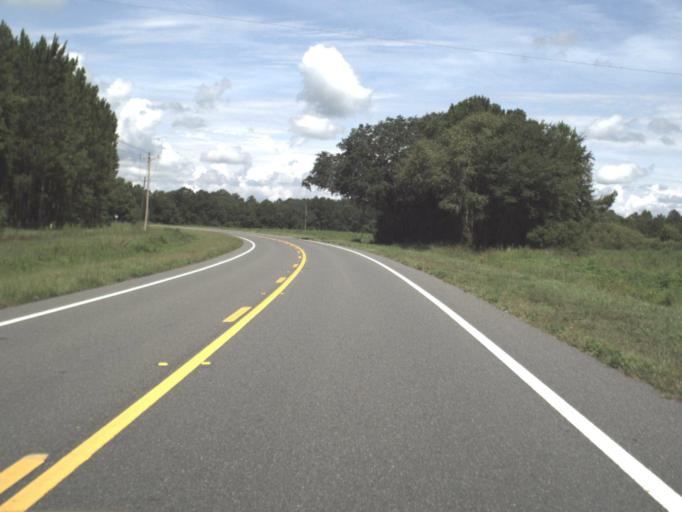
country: US
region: Florida
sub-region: Alachua County
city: Alachua
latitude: 29.8435
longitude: -82.3888
